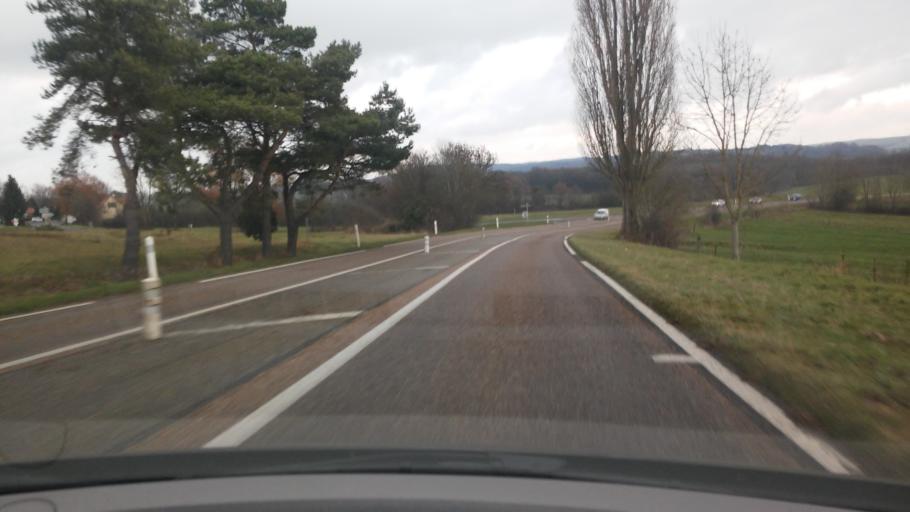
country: FR
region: Lorraine
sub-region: Departement de la Moselle
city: Courcelles-Chaussy
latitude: 49.1157
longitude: 6.3613
